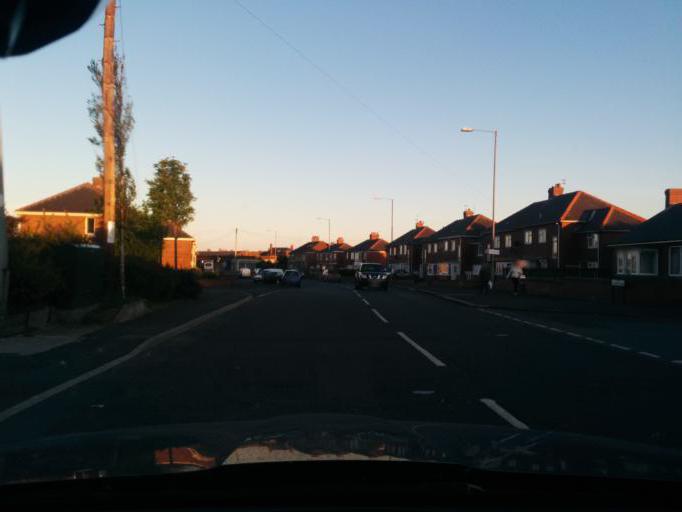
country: GB
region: England
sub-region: Northumberland
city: Newbiggin-by-the-Sea
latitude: 55.1893
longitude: -1.5219
